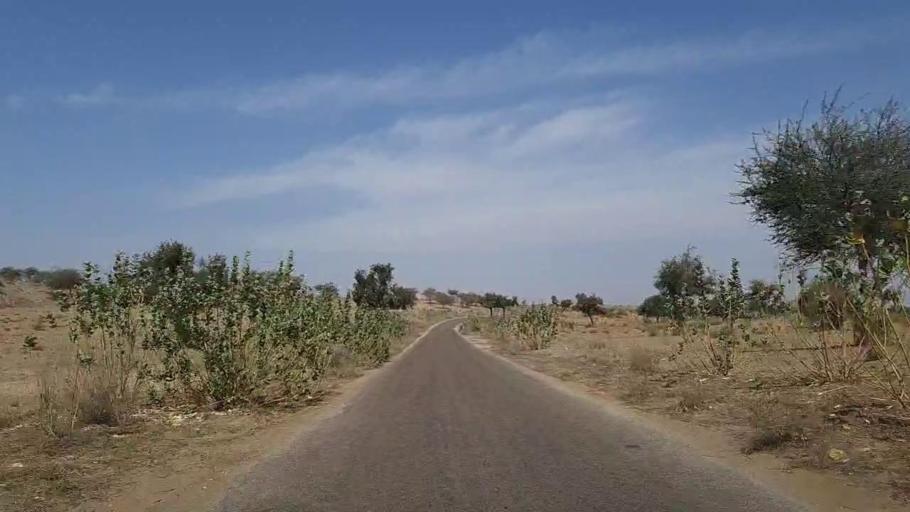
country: PK
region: Sindh
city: Umarkot
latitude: 25.1342
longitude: 70.0090
